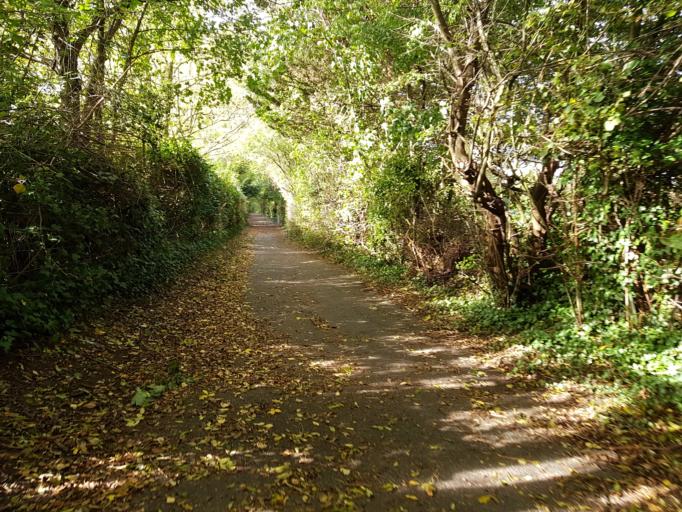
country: GB
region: England
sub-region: Isle of Wight
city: Ryde
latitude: 50.7294
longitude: -1.1767
